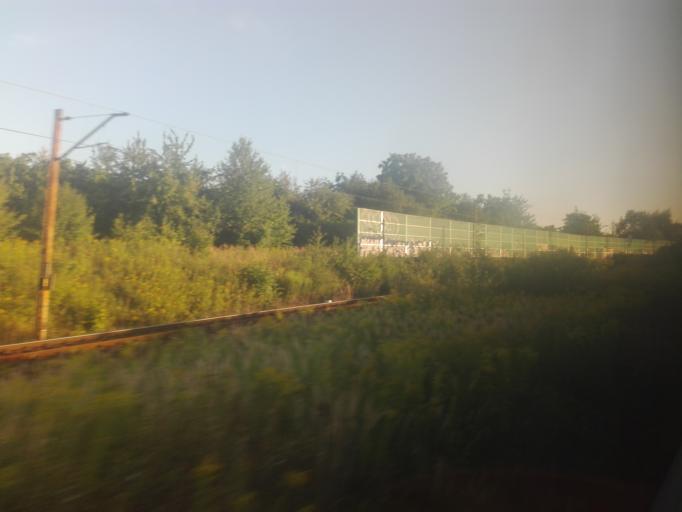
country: PL
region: Masovian Voivodeship
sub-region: Warszawa
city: Wlochy
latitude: 52.2129
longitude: 20.9374
